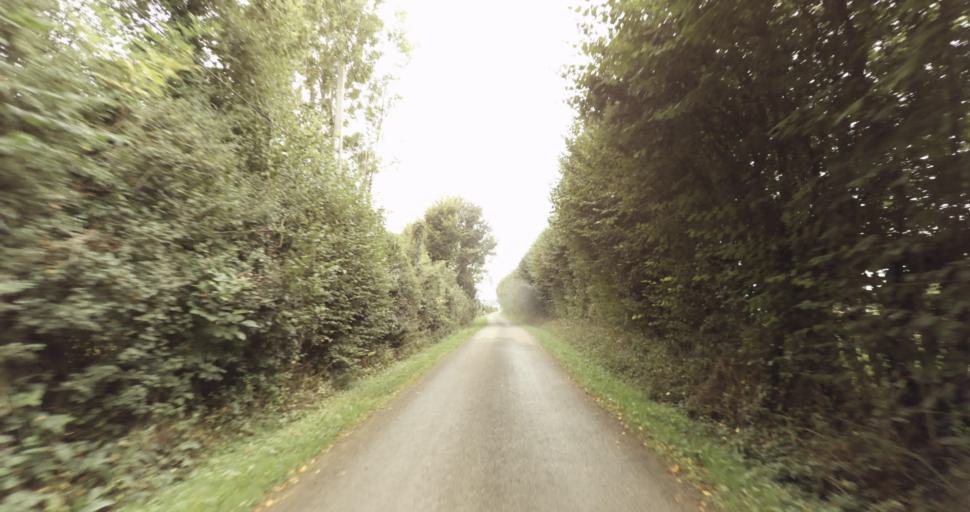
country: FR
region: Lower Normandy
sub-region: Departement de l'Orne
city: Sainte-Gauburge-Sainte-Colombe
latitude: 48.7331
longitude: 0.4208
